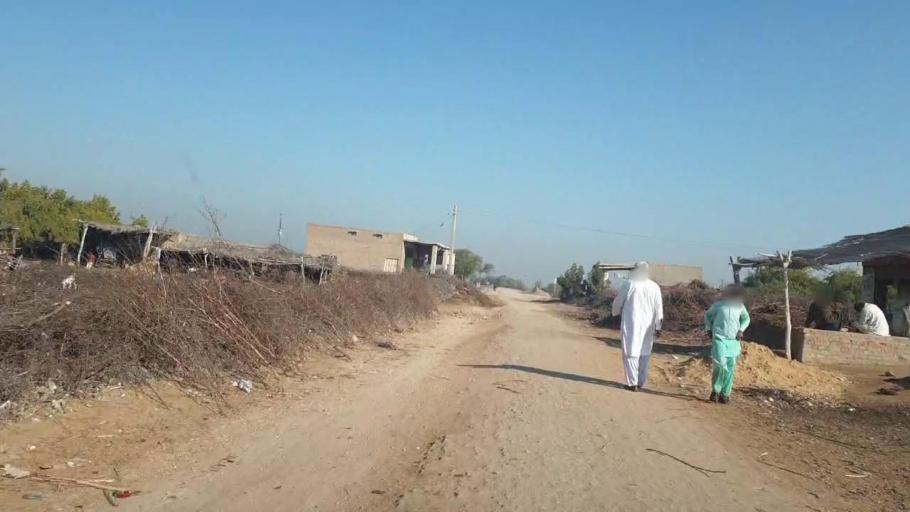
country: PK
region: Sindh
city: Shahdadpur
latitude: 25.9195
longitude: 68.5065
